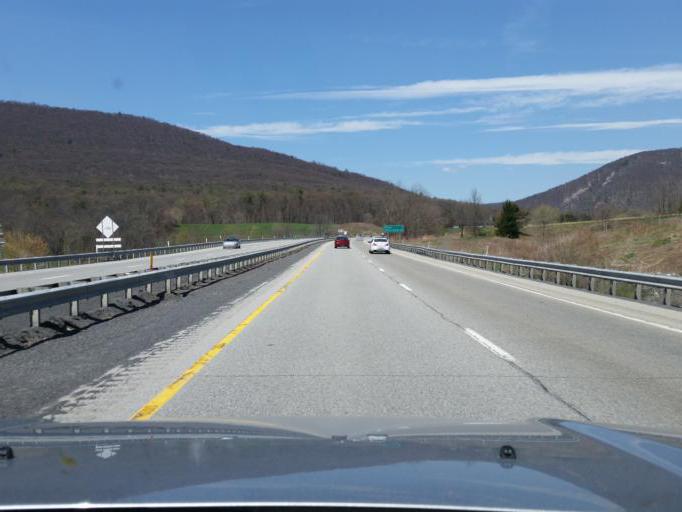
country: US
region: Pennsylvania
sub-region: Mifflin County
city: Yeagertown
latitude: 40.6343
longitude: -77.5843
